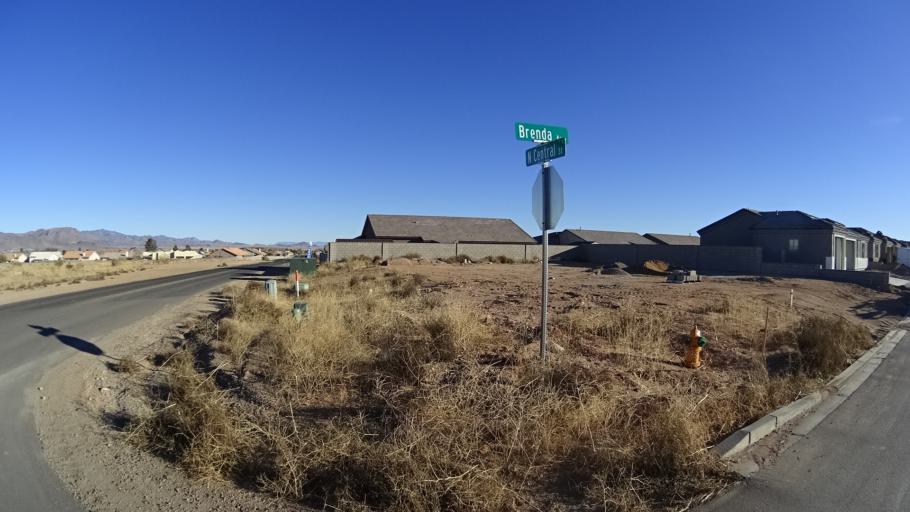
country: US
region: Arizona
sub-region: Mohave County
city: Kingman
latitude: 35.1908
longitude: -114.0026
